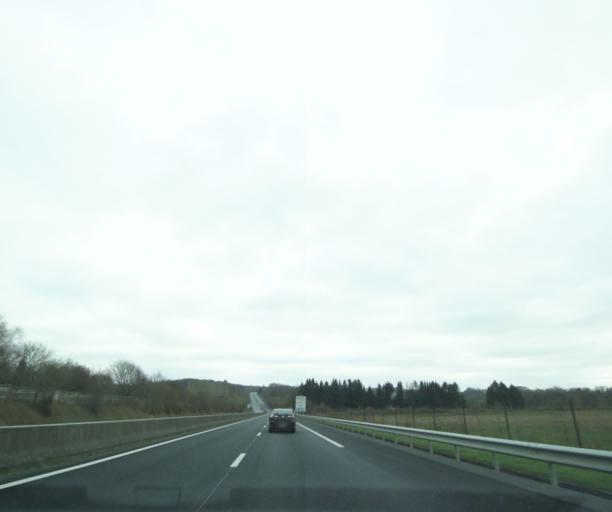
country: FR
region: Limousin
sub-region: Departement de la Correze
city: Uzerche
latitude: 45.3818
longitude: 1.5747
